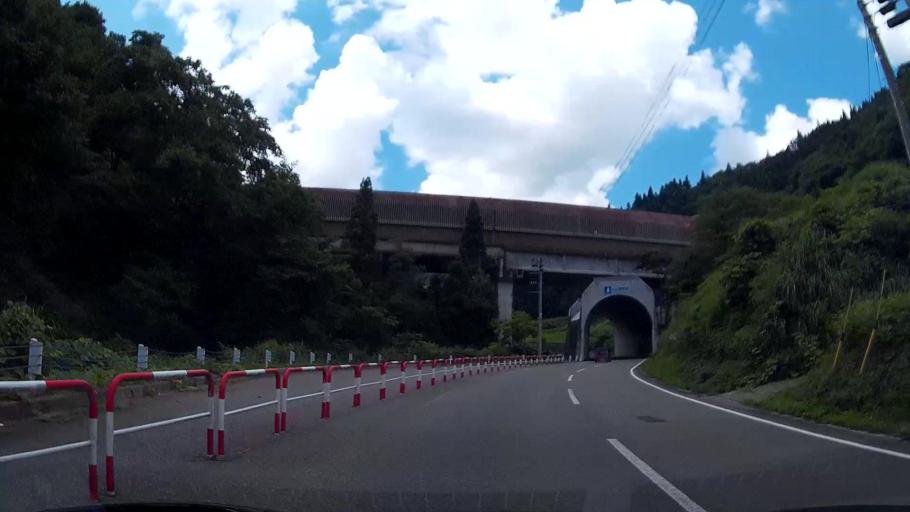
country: JP
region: Niigata
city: Shiozawa
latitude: 37.0208
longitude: 138.8139
